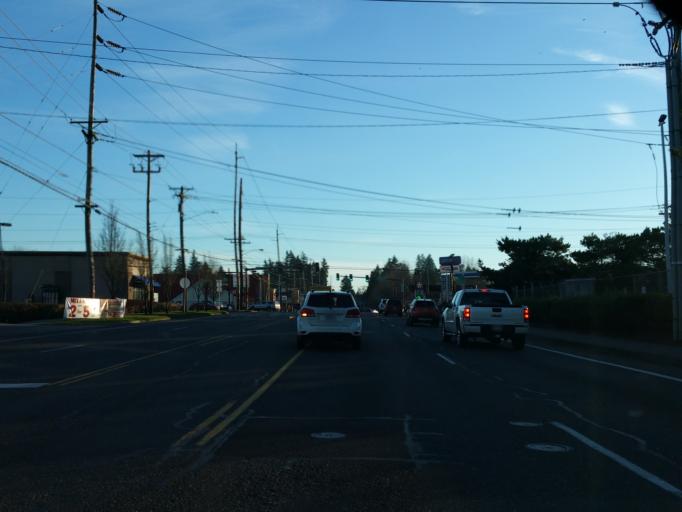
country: US
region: Oregon
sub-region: Multnomah County
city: Fairview
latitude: 45.5357
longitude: -122.4773
